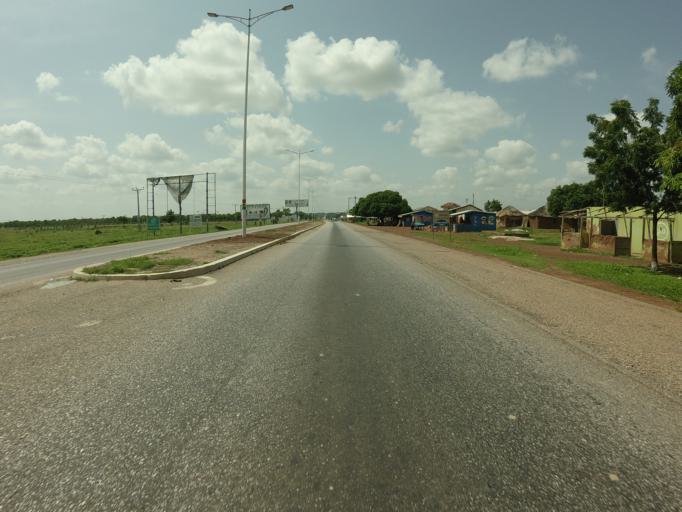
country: GH
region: Northern
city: Savelugu
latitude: 9.5505
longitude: -0.8377
